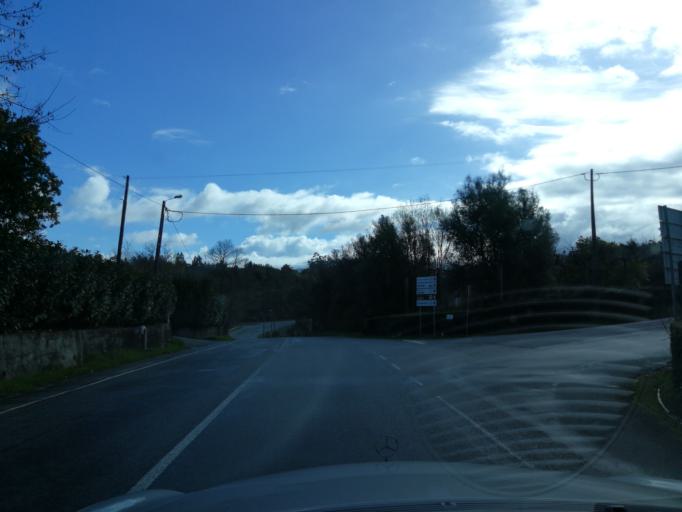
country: PT
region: Viana do Castelo
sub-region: Ponte da Barca
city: Ponte da Barca
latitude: 41.8099
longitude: -8.3588
